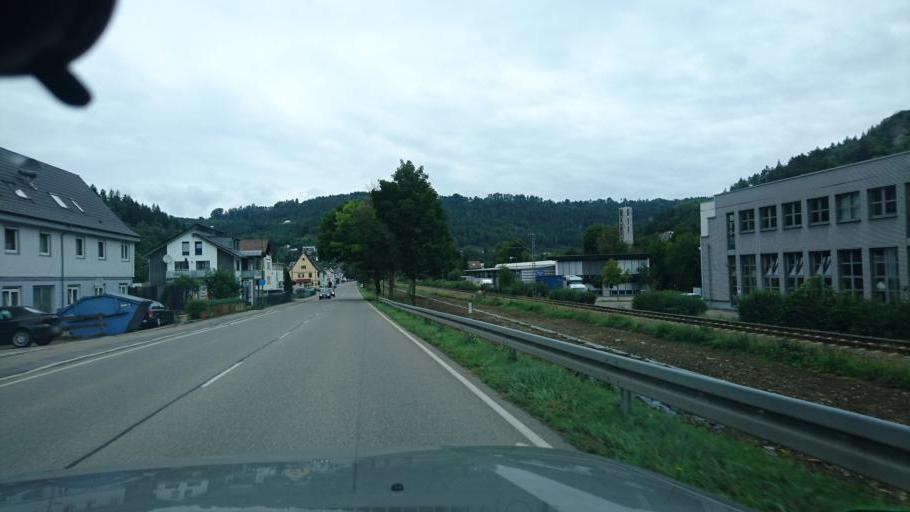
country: DE
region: Baden-Wuerttemberg
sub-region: Freiburg Region
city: Oberndorf
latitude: 48.3101
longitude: 8.5704
